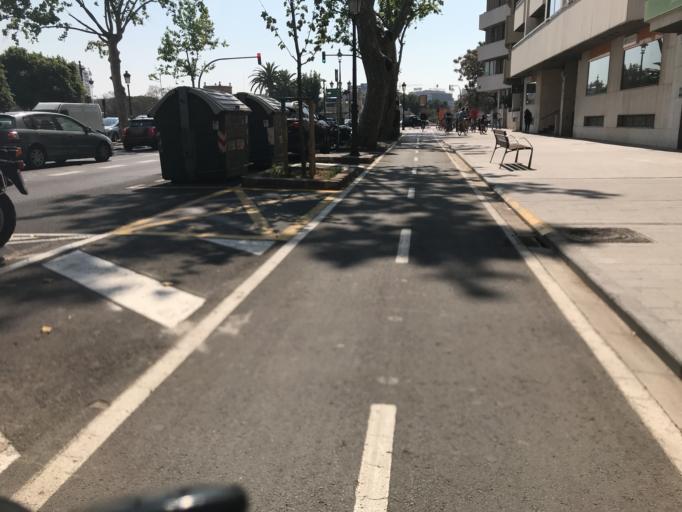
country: ES
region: Valencia
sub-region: Provincia de Valencia
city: Valencia
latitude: 39.4709
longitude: -0.3662
